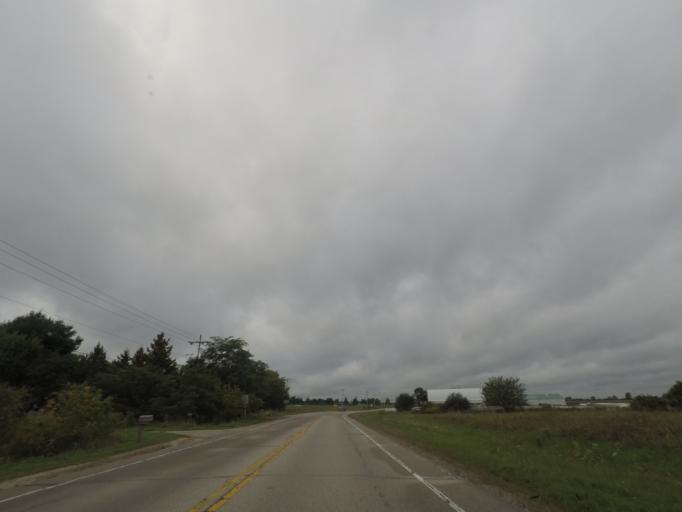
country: US
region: Wisconsin
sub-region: Waukesha County
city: Dousman
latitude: 43.0247
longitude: -88.5403
